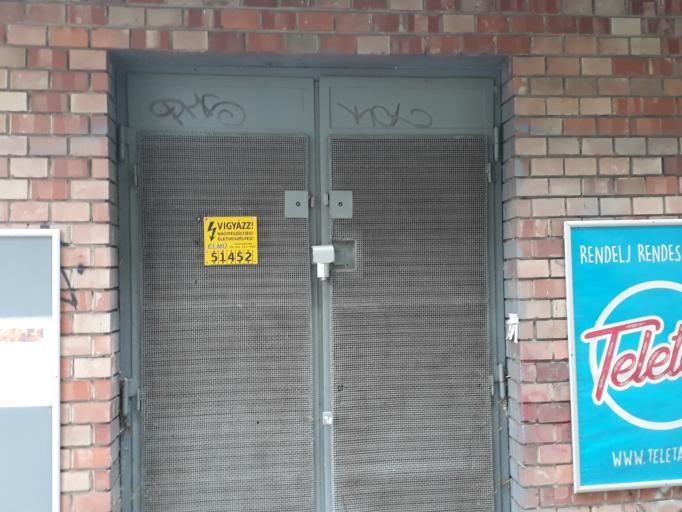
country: HU
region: Budapest
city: Budapest XI. keruelet
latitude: 47.4621
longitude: 19.0312
